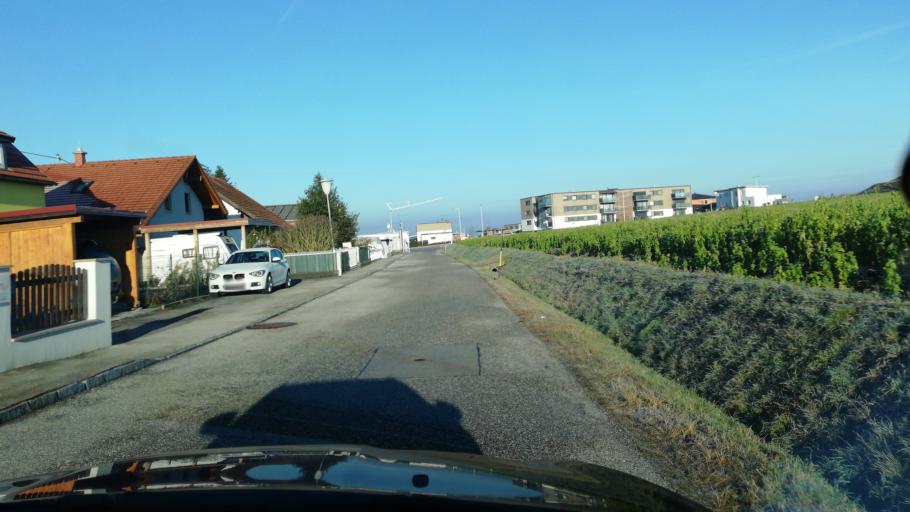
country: AT
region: Upper Austria
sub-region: Politischer Bezirk Steyr-Land
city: Bad Hall
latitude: 48.0355
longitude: 14.2151
